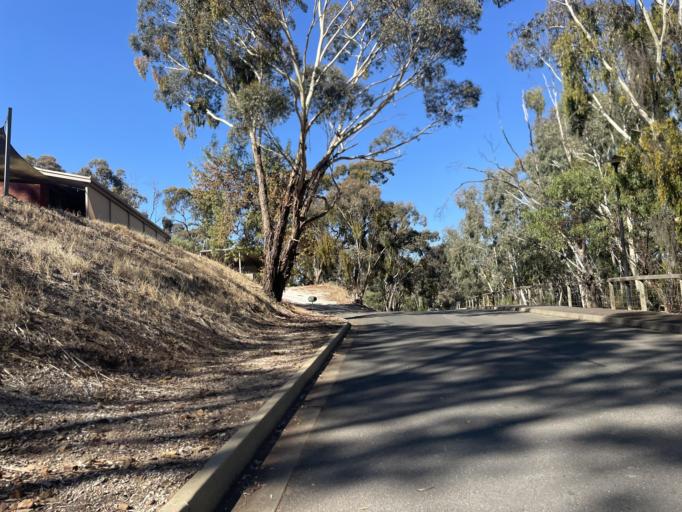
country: AU
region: South Australia
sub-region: Clare and Gilbert Valleys
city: Clare
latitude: -33.8428
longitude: 138.6133
